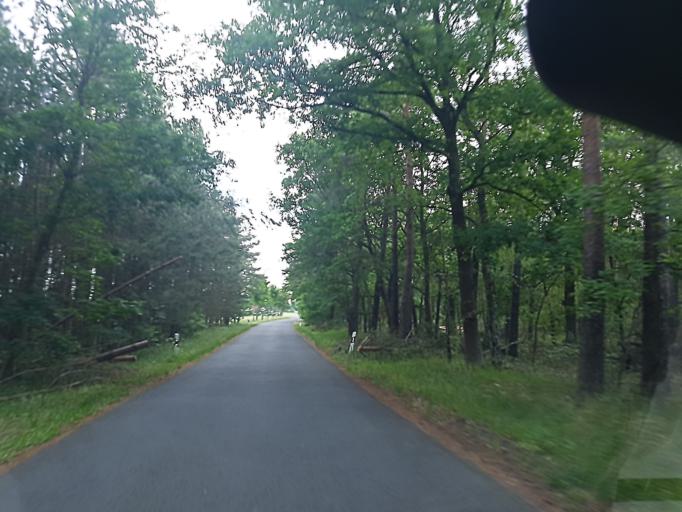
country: DE
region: Saxony-Anhalt
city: Holzdorf
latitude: 51.7724
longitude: 13.1113
